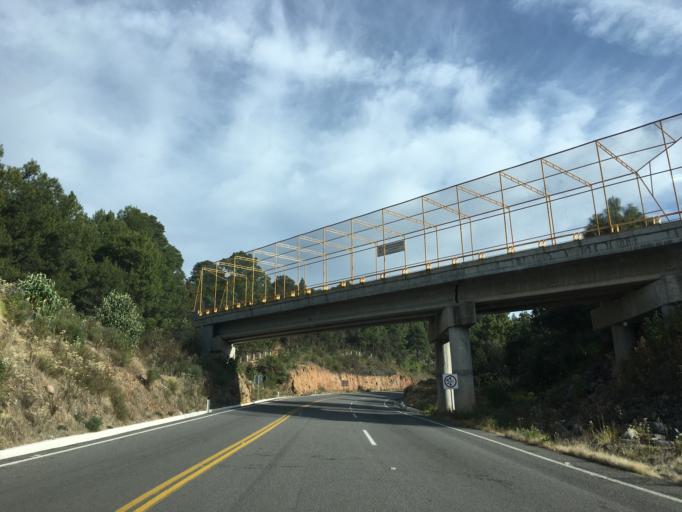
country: MX
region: Mexico
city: San Bartolo
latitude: 19.2632
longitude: -100.0650
